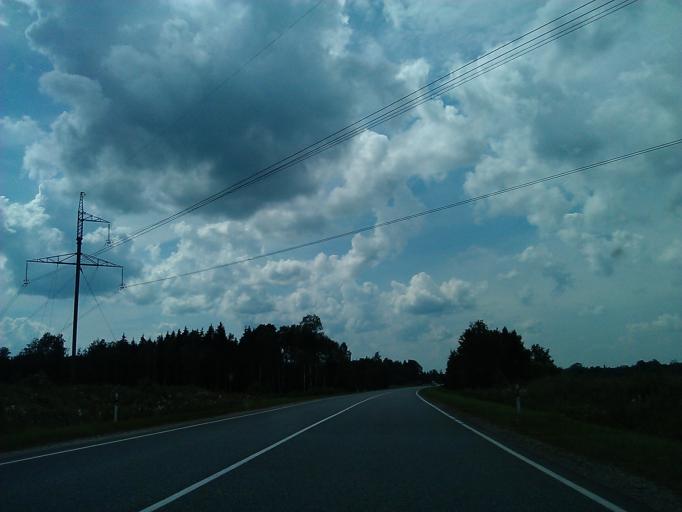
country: LV
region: Jaunpils
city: Jaunpils
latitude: 56.6624
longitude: 22.9956
